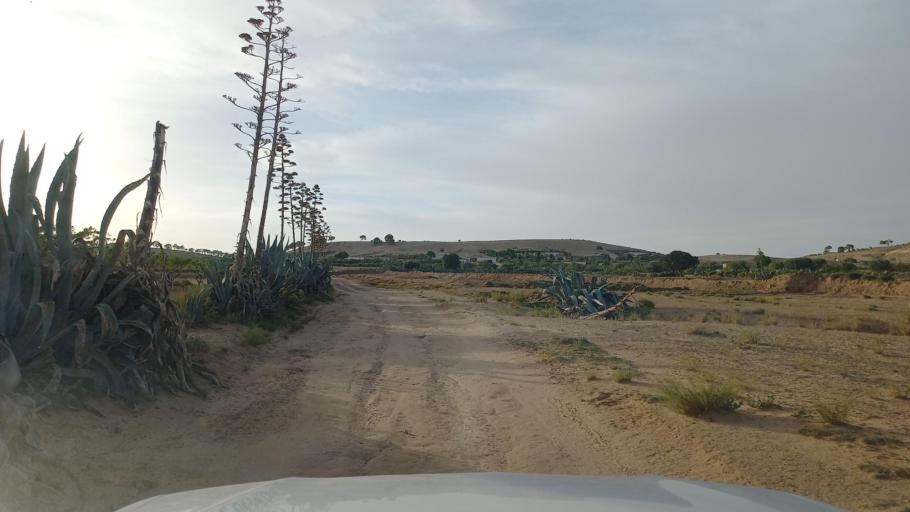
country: TN
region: Al Qasrayn
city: Sbiba
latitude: 35.4079
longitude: 8.9063
